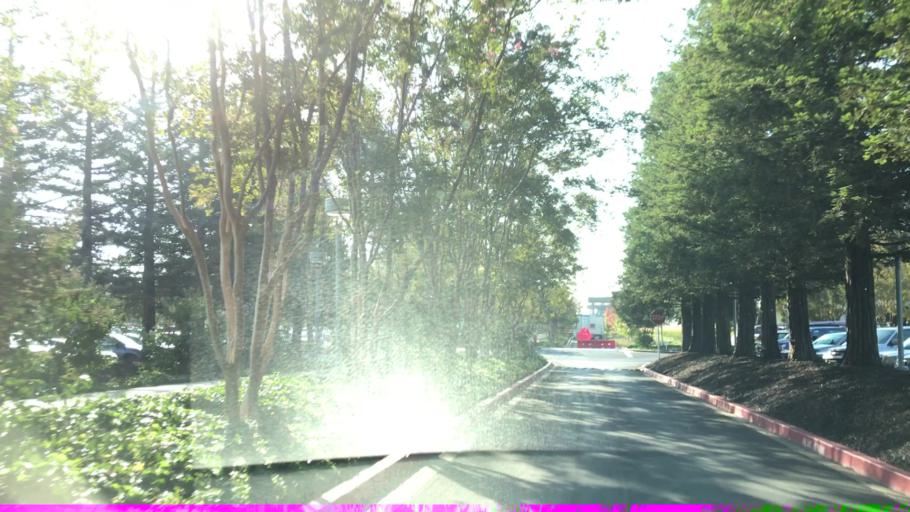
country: US
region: California
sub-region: Contra Costa County
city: San Ramon
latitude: 37.7657
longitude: -121.9613
